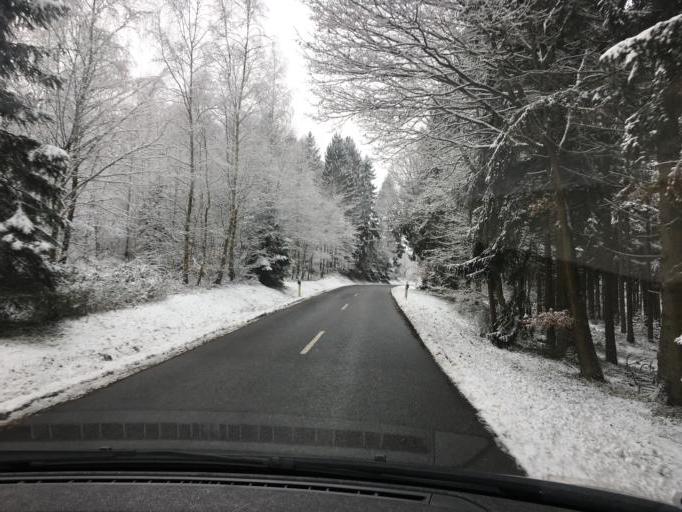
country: DE
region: North Rhine-Westphalia
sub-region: Regierungsbezirk Koln
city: Hurtgenwald
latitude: 50.7111
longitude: 6.4157
